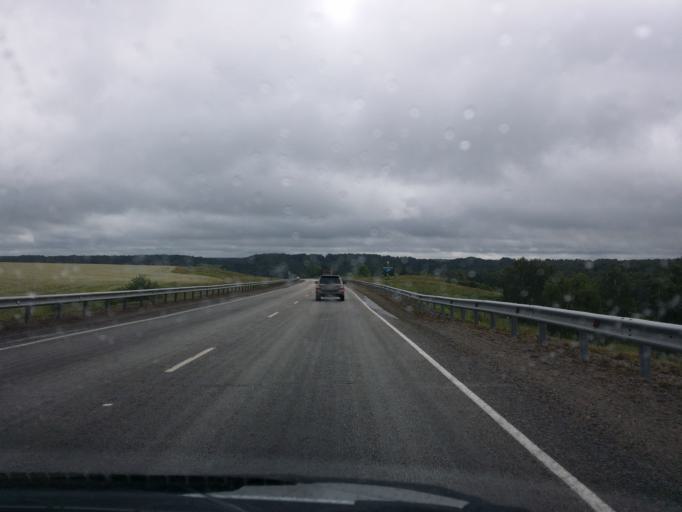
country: RU
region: Altai Krai
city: Nalobikha
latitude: 53.1578
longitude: 84.6748
